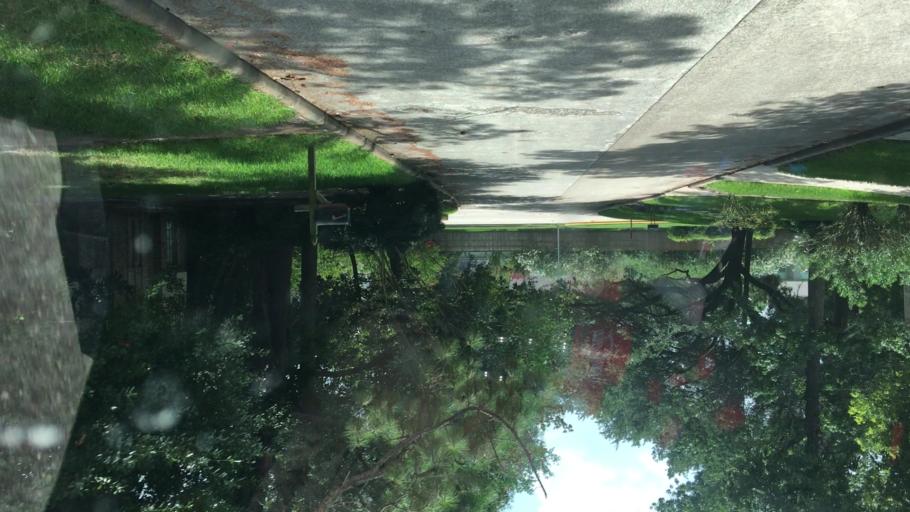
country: US
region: Texas
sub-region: Harris County
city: Atascocita
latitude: 30.0079
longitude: -95.1677
